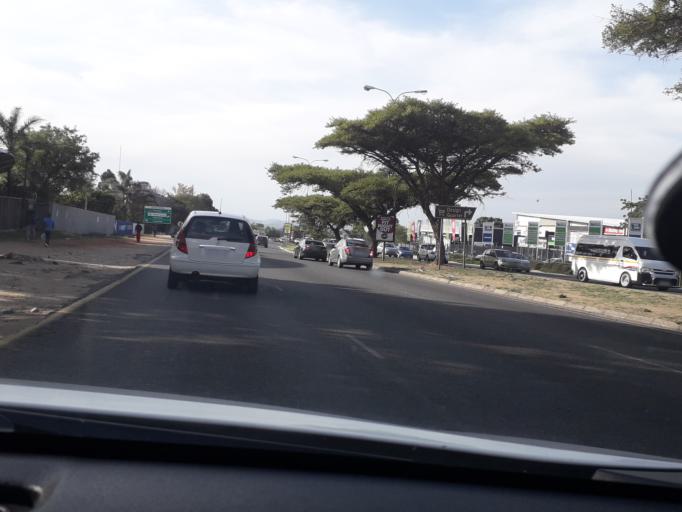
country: ZA
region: Gauteng
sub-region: City of Johannesburg Metropolitan Municipality
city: Diepsloot
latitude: -26.0351
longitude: 28.0108
